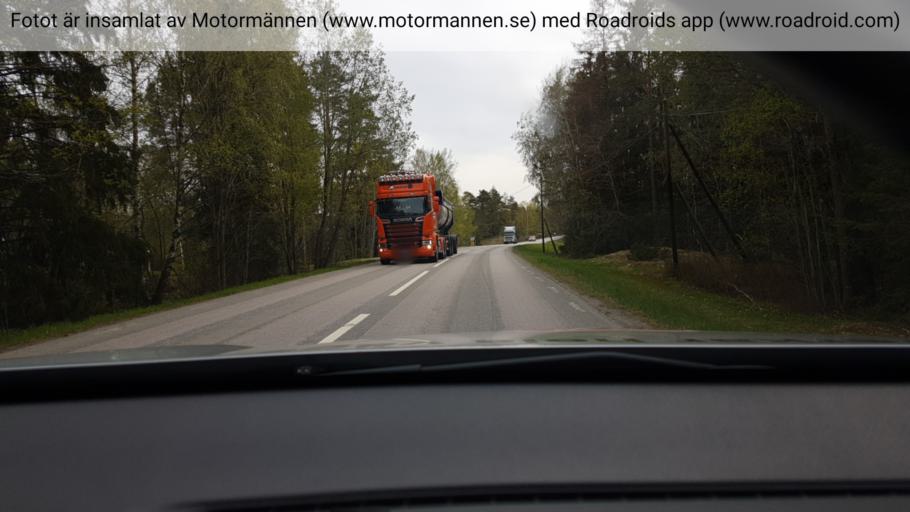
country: SE
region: Stockholm
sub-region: Norrtalje Kommun
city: Nykvarn
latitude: 59.9358
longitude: 18.1218
